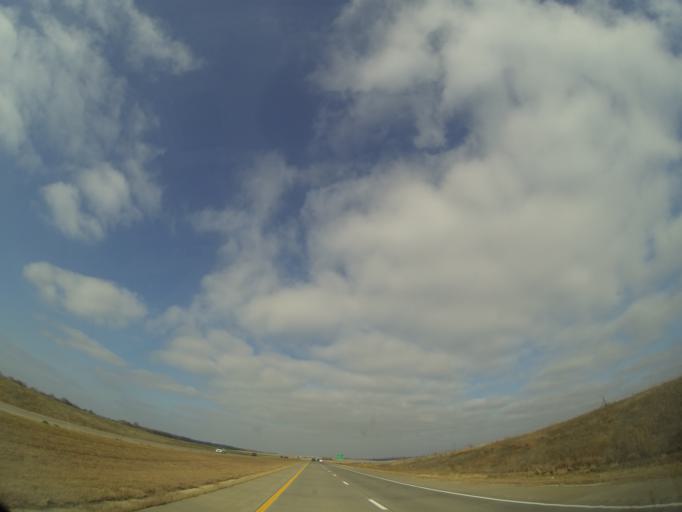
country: US
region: Kansas
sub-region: McPherson County
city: Lindsborg
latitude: 38.6596
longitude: -97.6216
